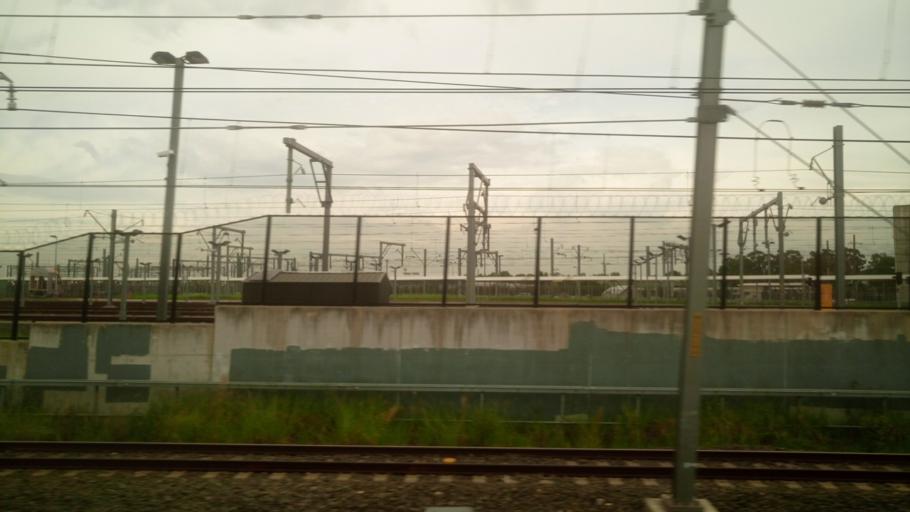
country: AU
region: New South Wales
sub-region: Parramatta
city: Granville
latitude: -33.8389
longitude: 151.0214
